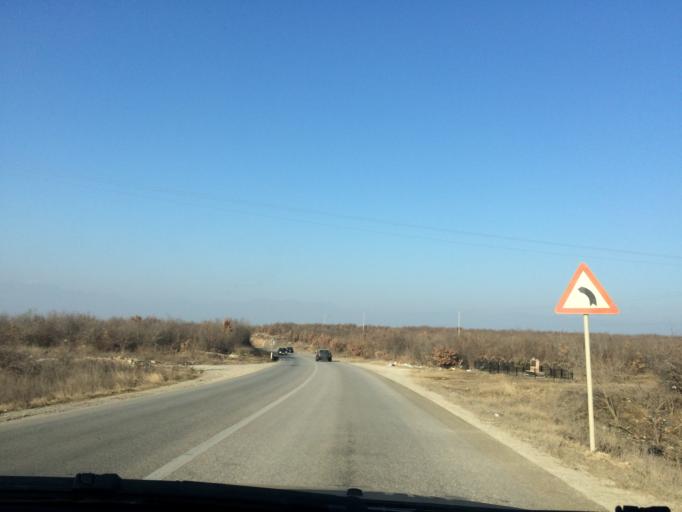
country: XK
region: Pec
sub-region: Komuna e Klines
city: Klina
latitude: 42.5967
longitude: 20.6267
